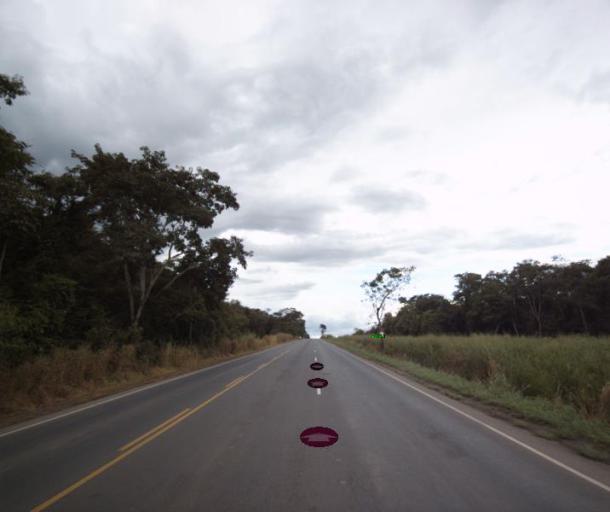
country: BR
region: Goias
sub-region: Itapaci
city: Itapaci
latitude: -14.9933
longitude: -49.4064
